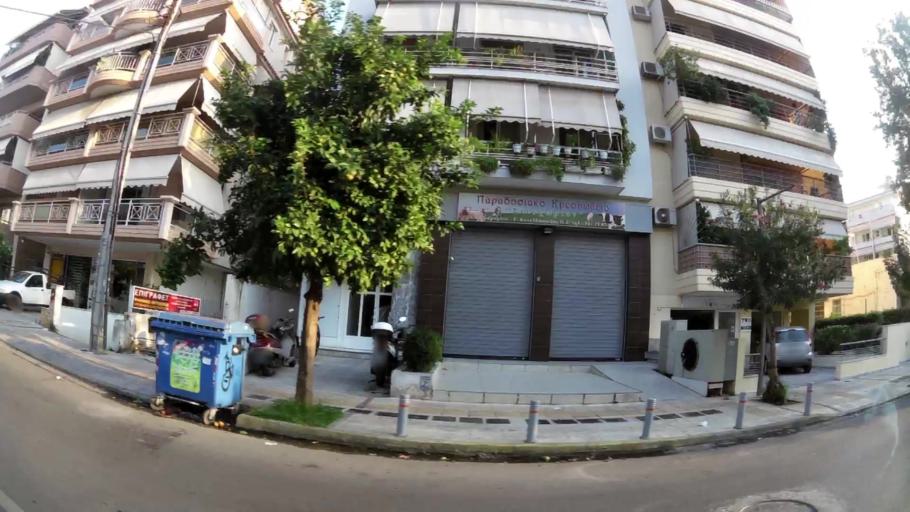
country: GR
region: Attica
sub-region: Nomarchia Athinas
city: Kallithea
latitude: 37.9587
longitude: 23.6944
